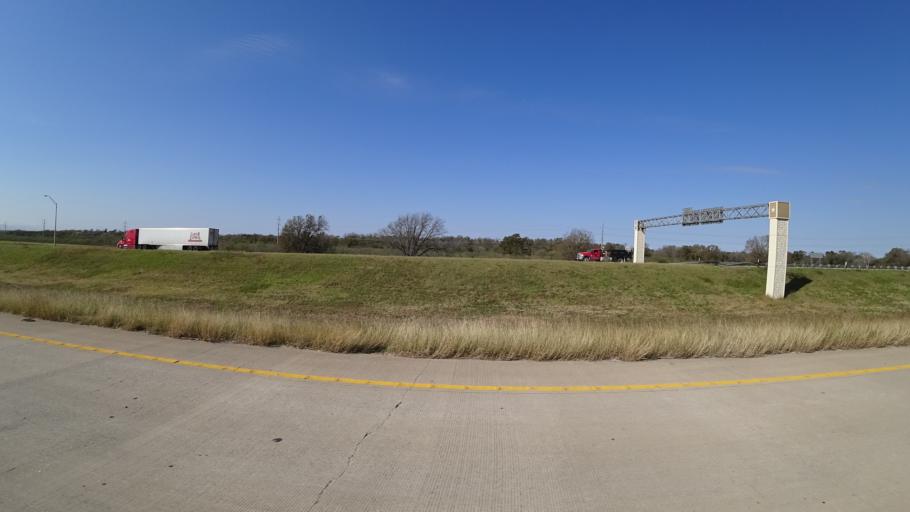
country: US
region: Texas
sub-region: Travis County
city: Garfield
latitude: 30.1840
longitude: -97.6289
